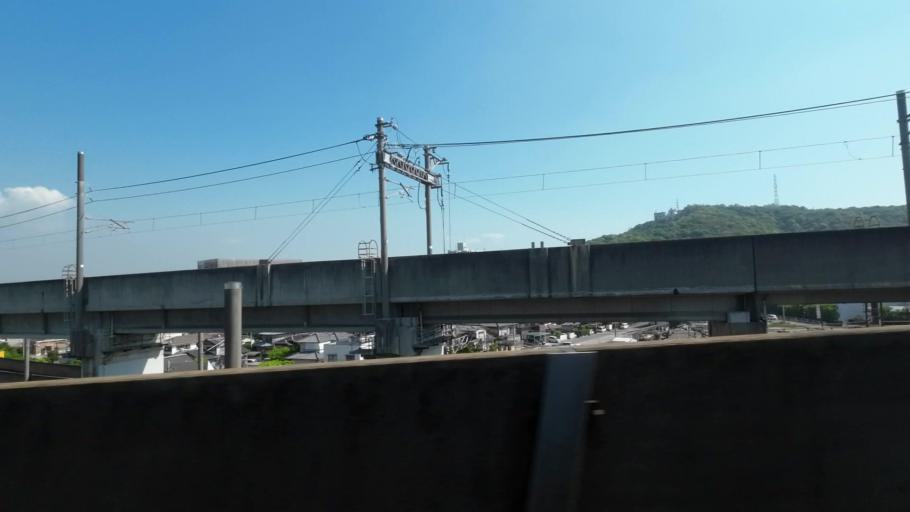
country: JP
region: Kagawa
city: Sakaidecho
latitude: 34.3139
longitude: 133.8243
